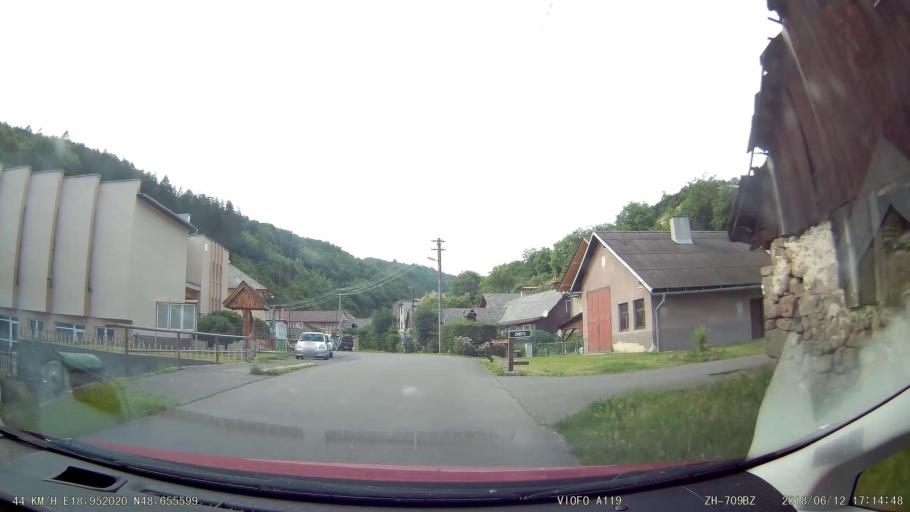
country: SK
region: Banskobystricky
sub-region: Okres Ziar nad Hronom
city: Kremnica
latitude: 48.6558
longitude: 18.9519
